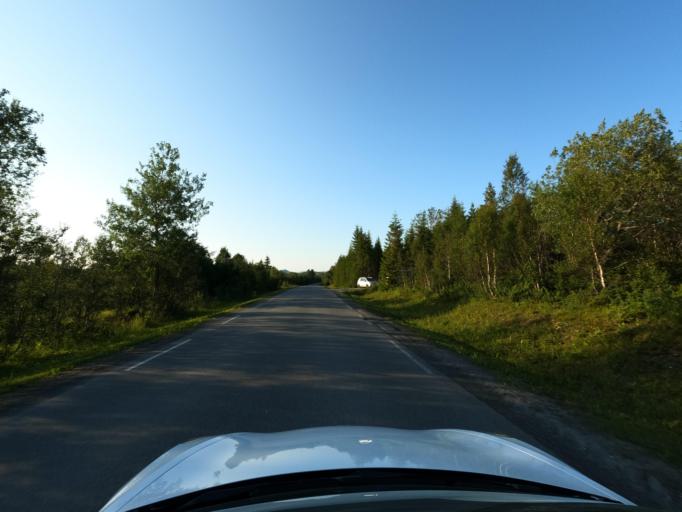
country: NO
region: Troms
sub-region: Skanland
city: Evenskjer
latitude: 68.4833
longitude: 16.7115
